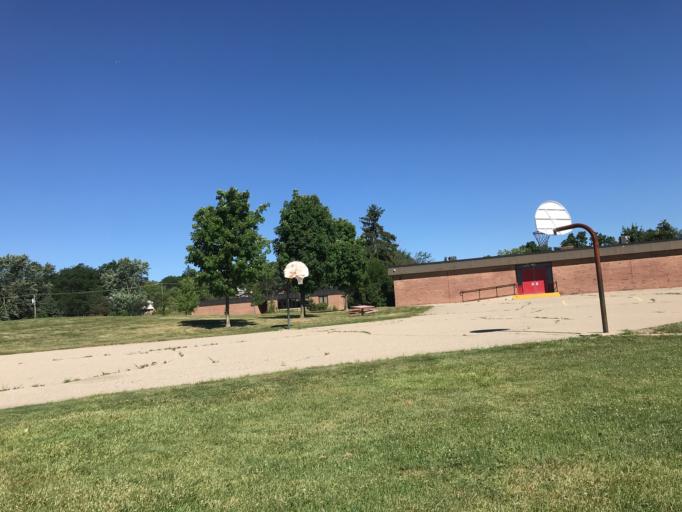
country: US
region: Michigan
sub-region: Washtenaw County
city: Ann Arbor
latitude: 42.2505
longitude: -83.7103
